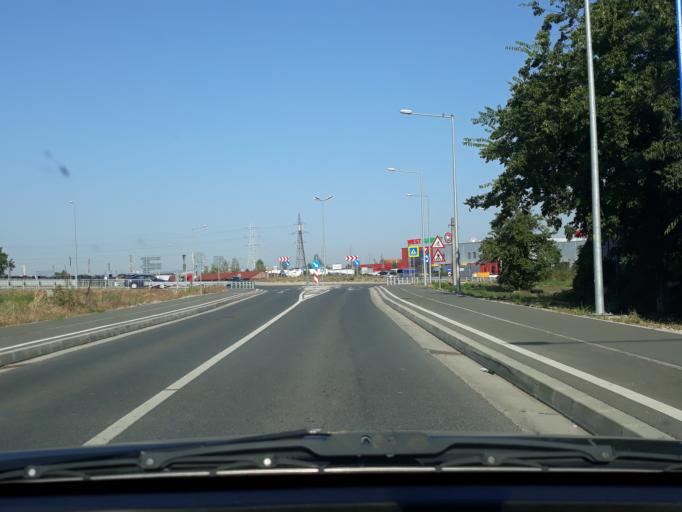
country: RO
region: Bihor
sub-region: Comuna Sanmartin
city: Sanmartin
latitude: 47.0290
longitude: 21.9451
